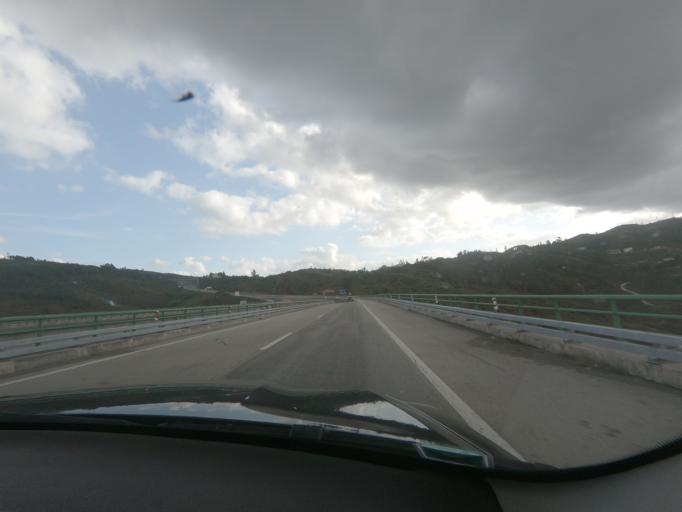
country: PT
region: Viseu
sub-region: Castro Daire
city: Castro Daire
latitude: 40.8896
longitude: -7.9199
